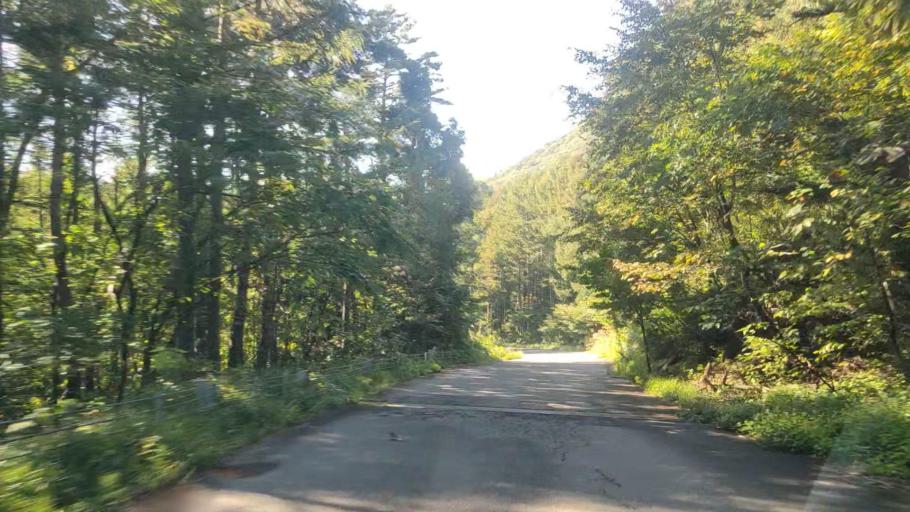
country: JP
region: Nagano
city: Iiyama
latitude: 36.8096
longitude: 138.4249
